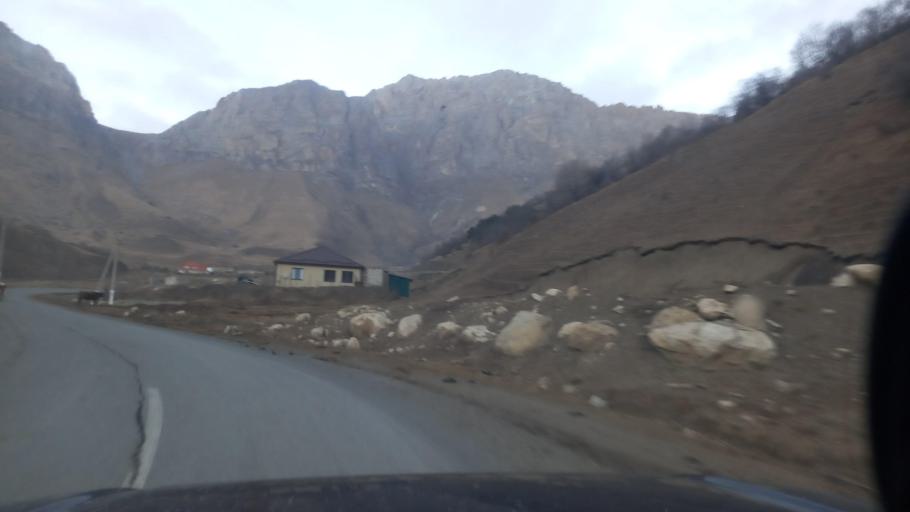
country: RU
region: Ingushetiya
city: Dzhayrakh
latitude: 42.8161
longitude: 44.8145
